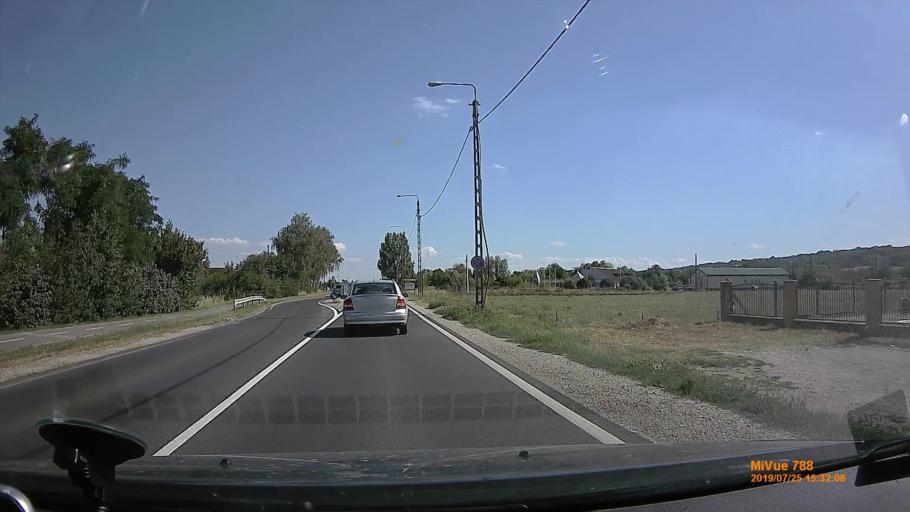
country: HU
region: Borsod-Abauj-Zemplen
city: Malyi
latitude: 48.0087
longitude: 20.8270
